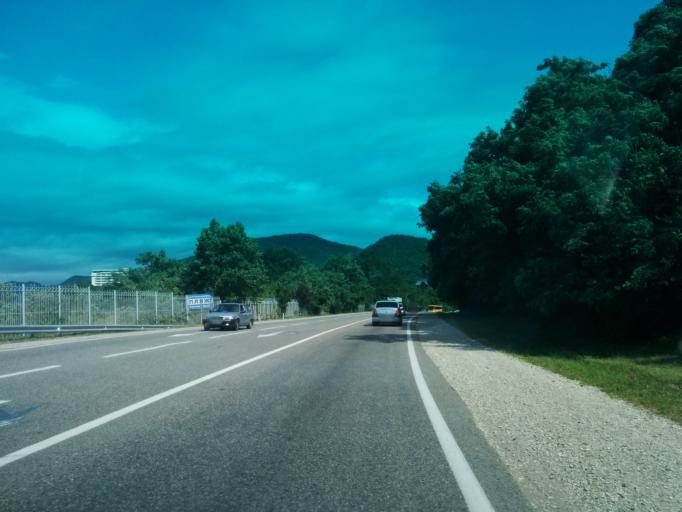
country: RU
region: Krasnodarskiy
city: Nebug
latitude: 44.1586
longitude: 39.0022
